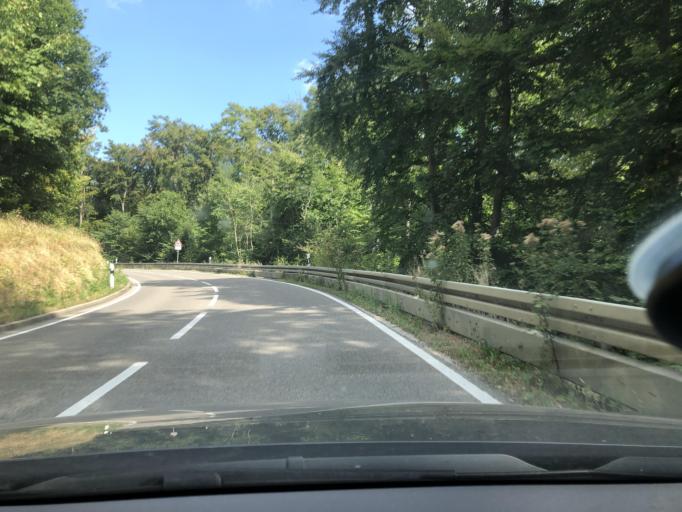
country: DE
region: Baden-Wuerttemberg
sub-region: Tuebingen Region
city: Pfullingen
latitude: 48.4347
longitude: 9.2042
